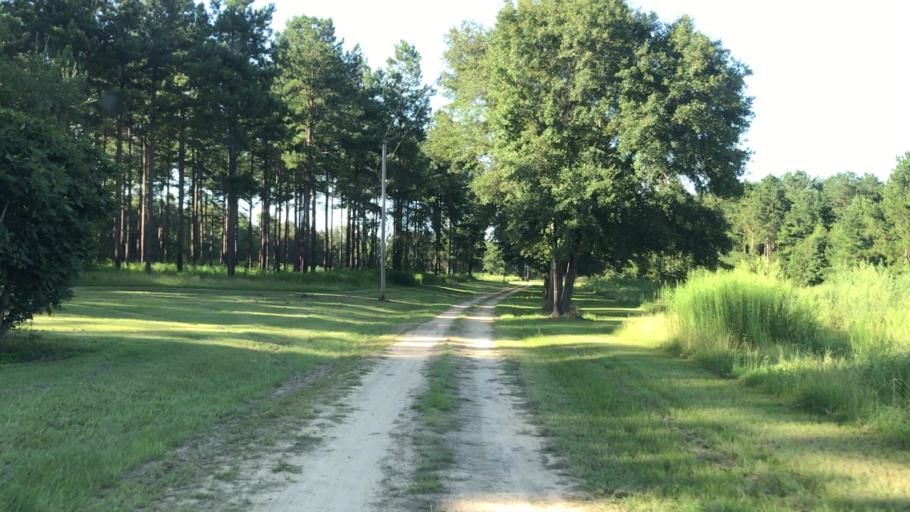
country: US
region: Georgia
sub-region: Jefferson County
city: Wadley
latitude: 32.8129
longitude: -82.3341
